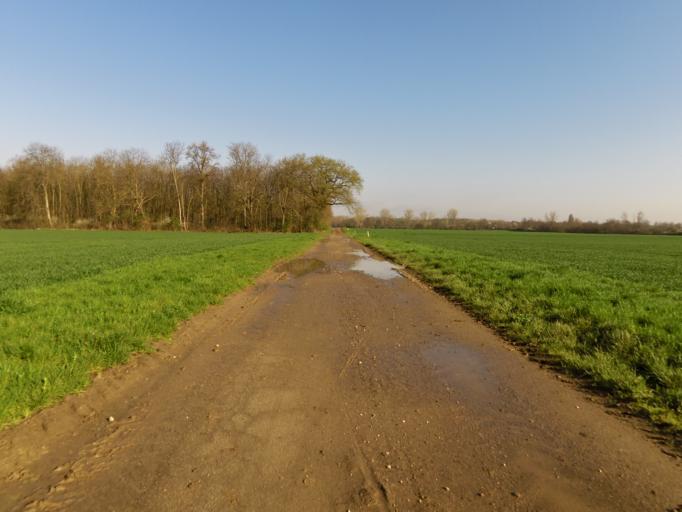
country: DE
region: Rheinland-Pfalz
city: Bobenheim-Roxheim
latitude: 49.5941
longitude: 8.3963
